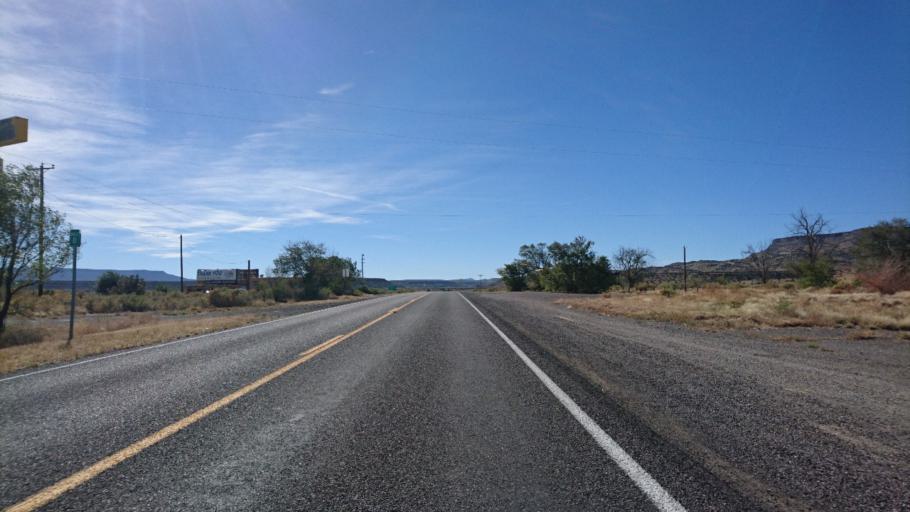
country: US
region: New Mexico
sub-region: Cibola County
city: Skyline-Ganipa
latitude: 35.0773
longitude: -107.6462
